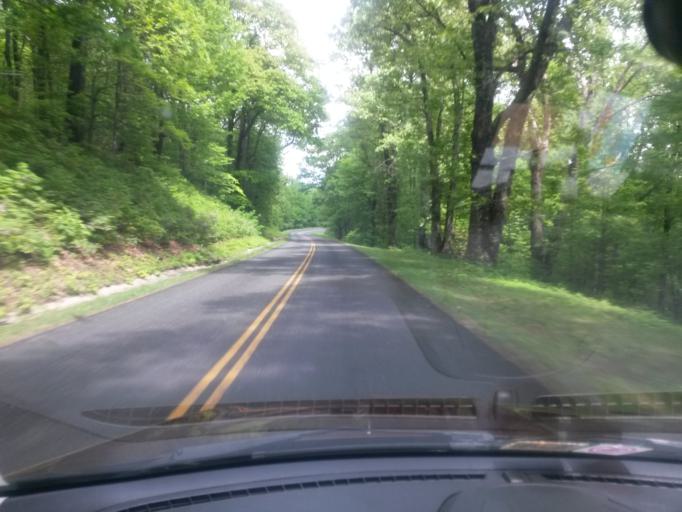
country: US
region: Virginia
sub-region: Floyd County
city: Floyd
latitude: 36.8319
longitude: -80.3376
